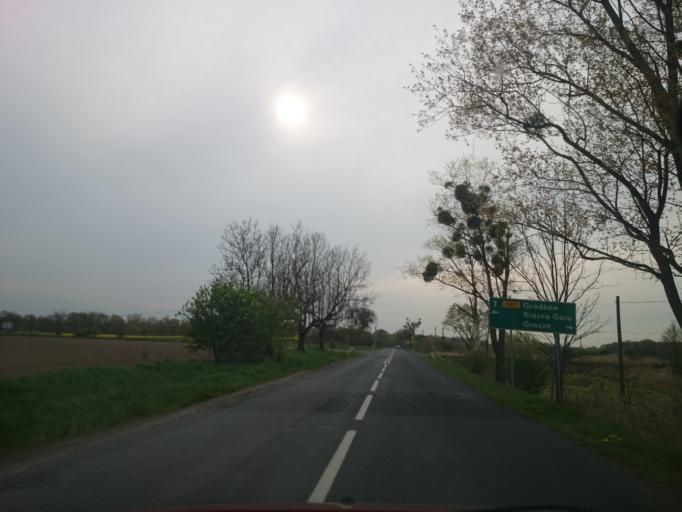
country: PL
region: Opole Voivodeship
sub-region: Powiat nyski
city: Sidzina
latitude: 50.6429
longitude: 17.4925
